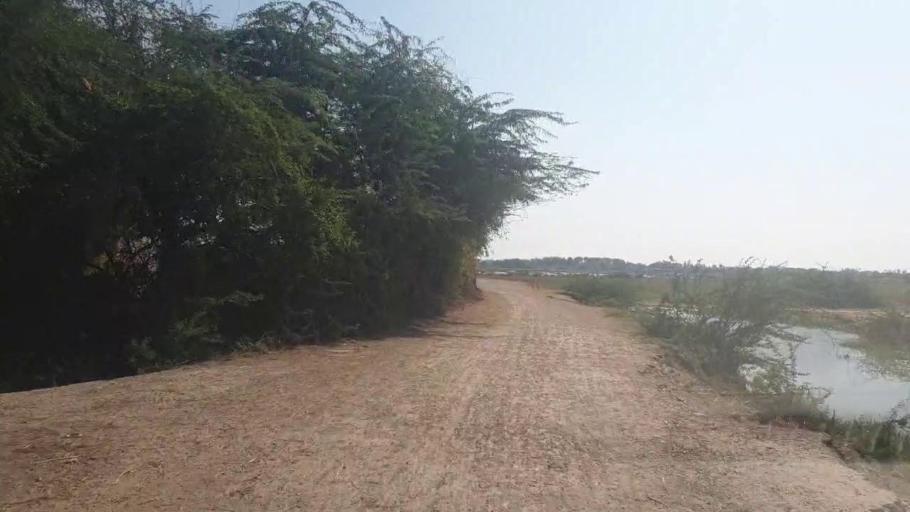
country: PK
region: Sindh
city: Badin
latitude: 24.5555
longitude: 68.8458
